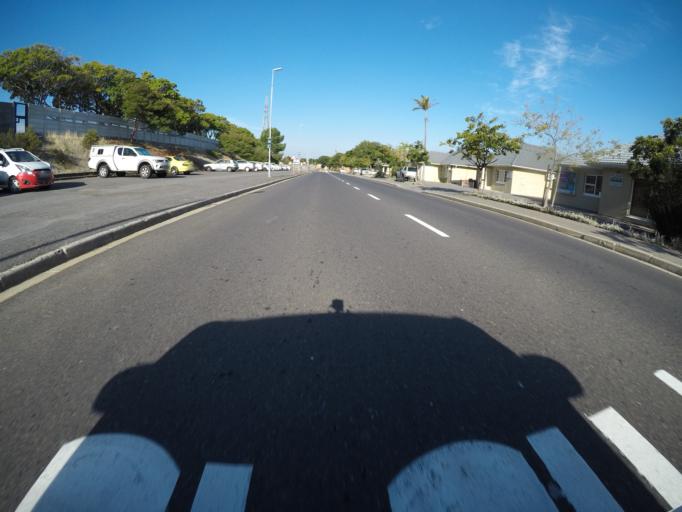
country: ZA
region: Western Cape
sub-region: City of Cape Town
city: Kraaifontein
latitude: -33.8805
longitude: 18.6391
